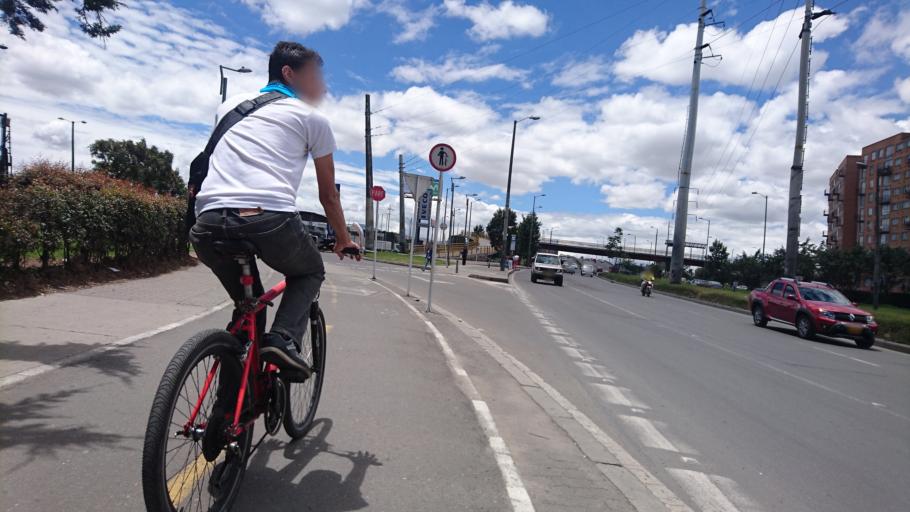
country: CO
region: Bogota D.C.
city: Bogota
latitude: 4.6615
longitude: -74.1338
